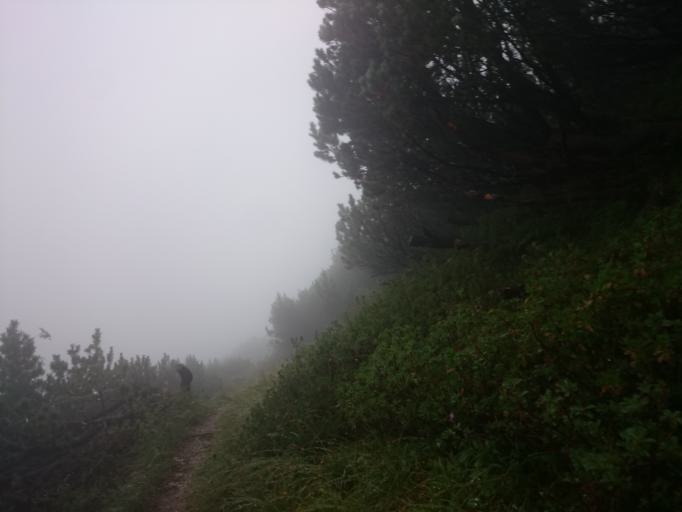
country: AT
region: Tyrol
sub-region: Politischer Bezirk Innsbruck Land
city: Absam
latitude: 47.4121
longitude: 11.5028
